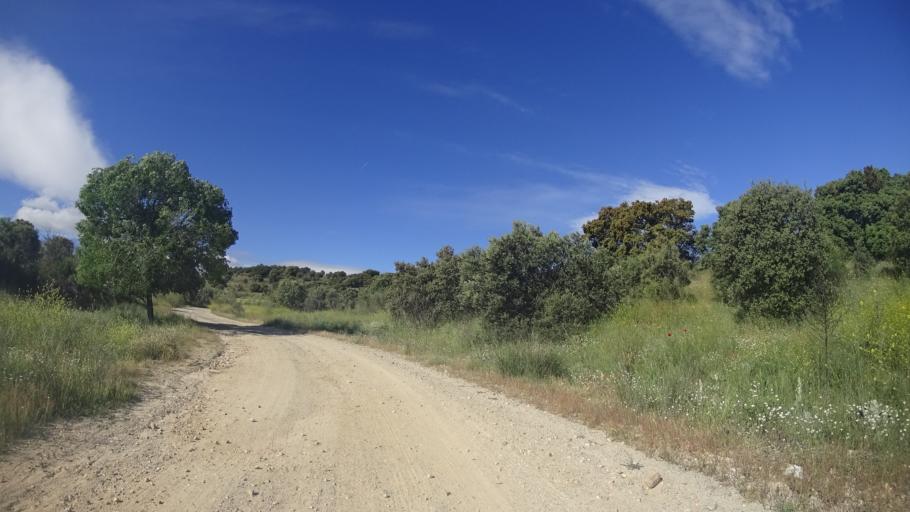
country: ES
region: Madrid
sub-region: Provincia de Madrid
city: Villanueva del Pardillo
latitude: 40.5073
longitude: -3.9398
